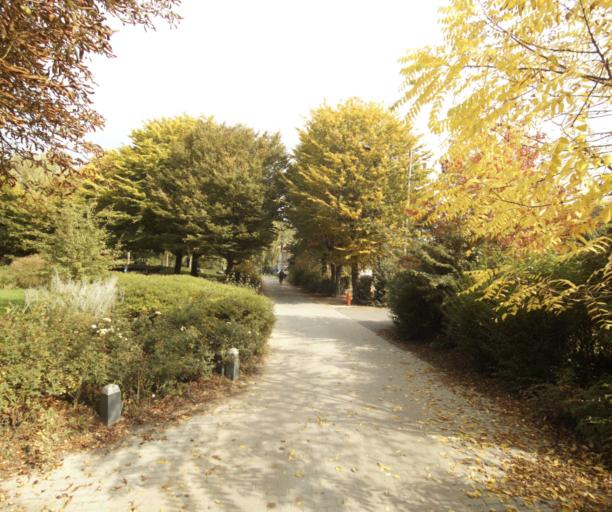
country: FR
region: Nord-Pas-de-Calais
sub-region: Departement du Nord
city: Haubourdin
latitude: 50.6148
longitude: 2.9883
